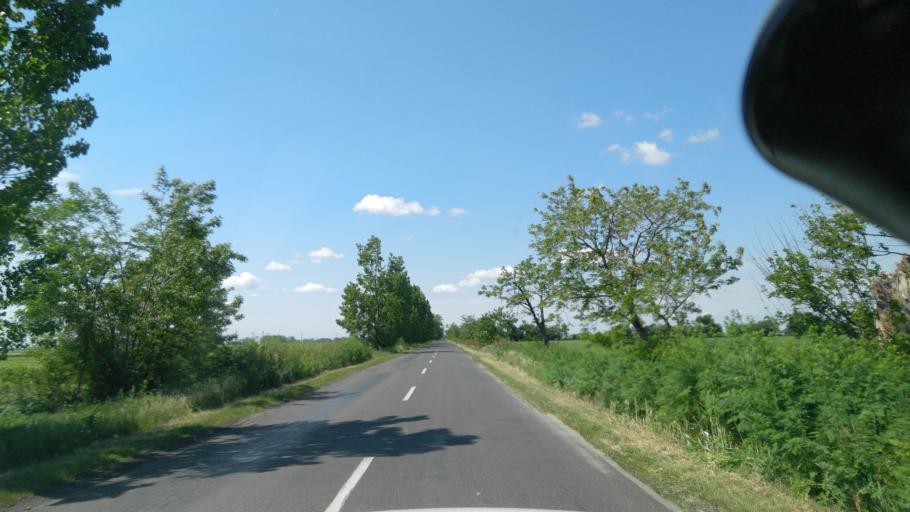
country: HU
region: Bekes
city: Medgyesegyhaza
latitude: 46.4649
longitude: 21.0101
